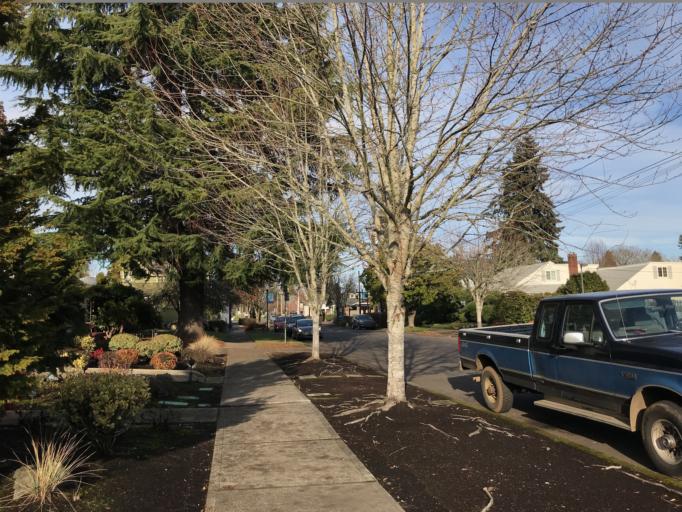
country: US
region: Oregon
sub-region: Washington County
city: Hillsboro
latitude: 45.5204
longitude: -122.9827
